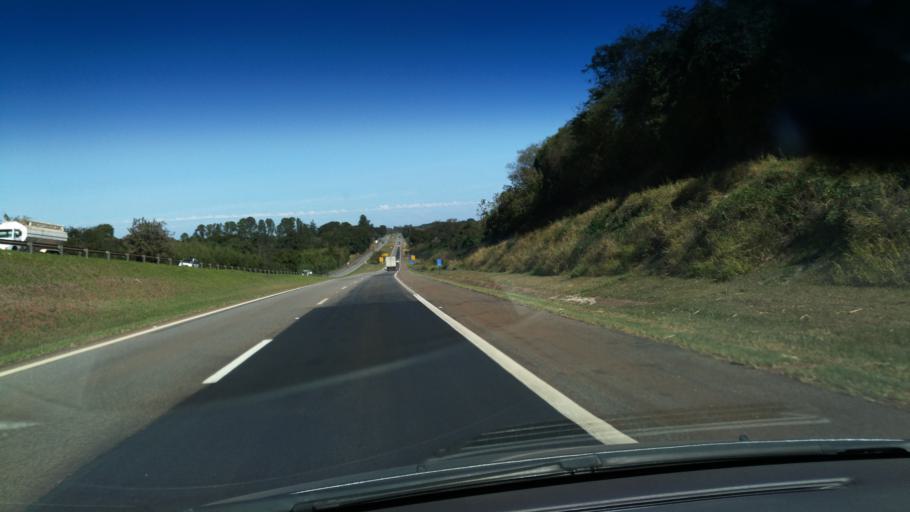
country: BR
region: Sao Paulo
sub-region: Santo Antonio De Posse
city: Santo Antonio de Posse
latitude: -22.5547
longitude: -46.9990
